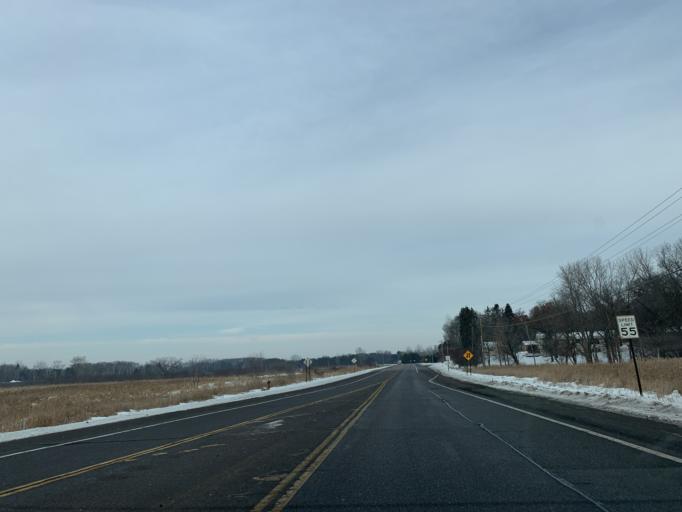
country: US
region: Minnesota
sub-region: Washington County
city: Forest Lake
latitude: 45.2829
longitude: -93.0121
